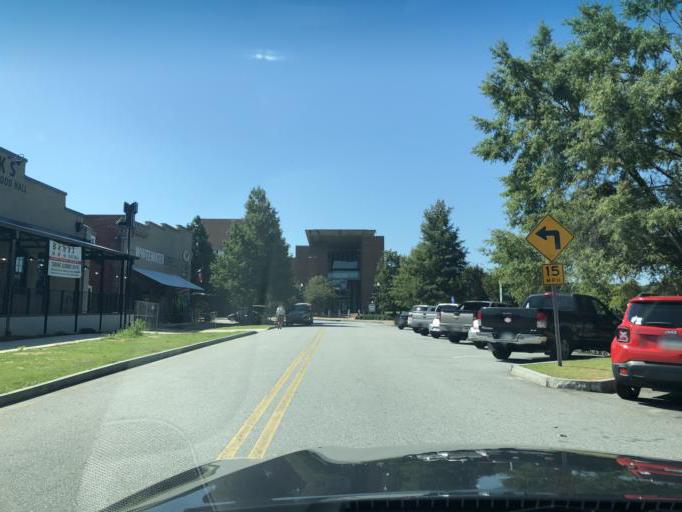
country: US
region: Alabama
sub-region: Russell County
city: Phenix City
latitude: 32.4655
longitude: -84.9960
